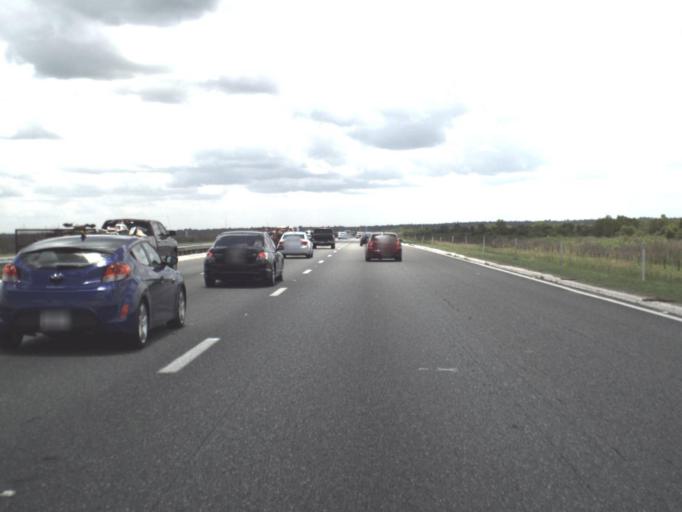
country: US
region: Florida
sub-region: Alachua County
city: Gainesville
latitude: 29.5860
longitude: -82.3603
